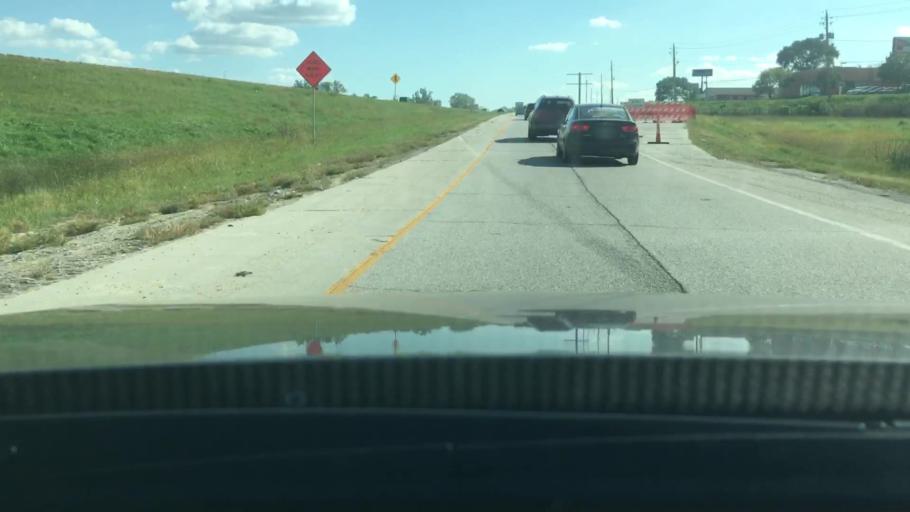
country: US
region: Iowa
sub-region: Pottawattamie County
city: Council Bluffs
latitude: 41.2419
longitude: -95.8253
